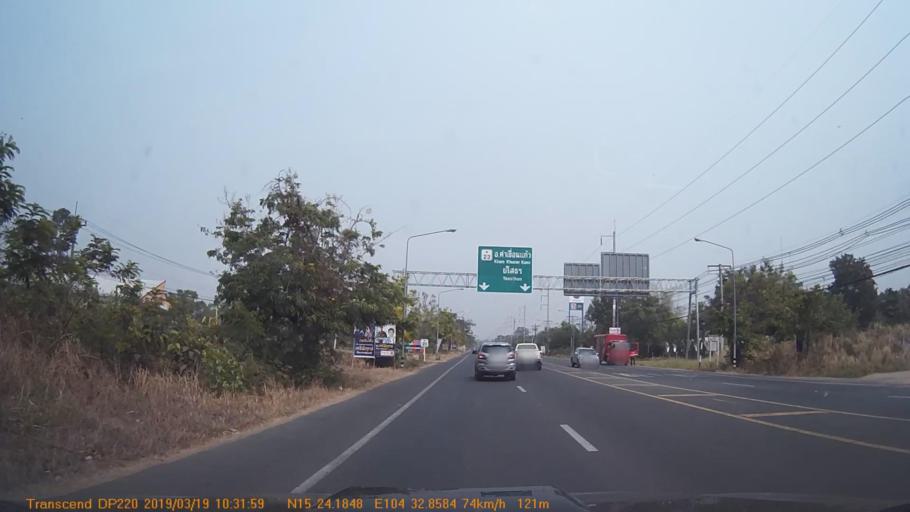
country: TH
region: Changwat Ubon Ratchathani
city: Khueang Nai
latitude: 15.4033
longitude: 104.5475
